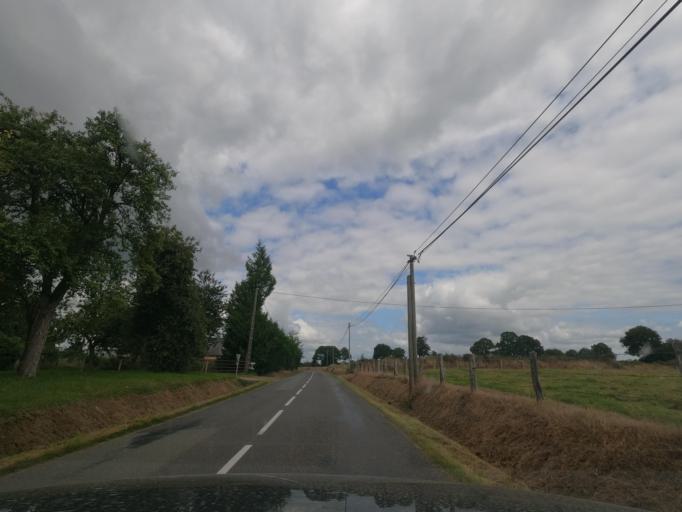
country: FR
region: Lower Normandy
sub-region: Departement de la Manche
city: Le Teilleul
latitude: 48.5159
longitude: -0.8968
